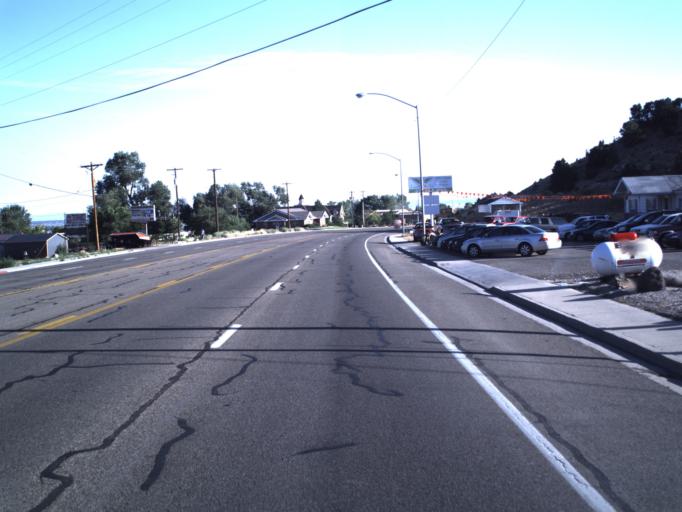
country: US
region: Utah
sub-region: Iron County
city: Cedar City
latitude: 37.6973
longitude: -113.0634
